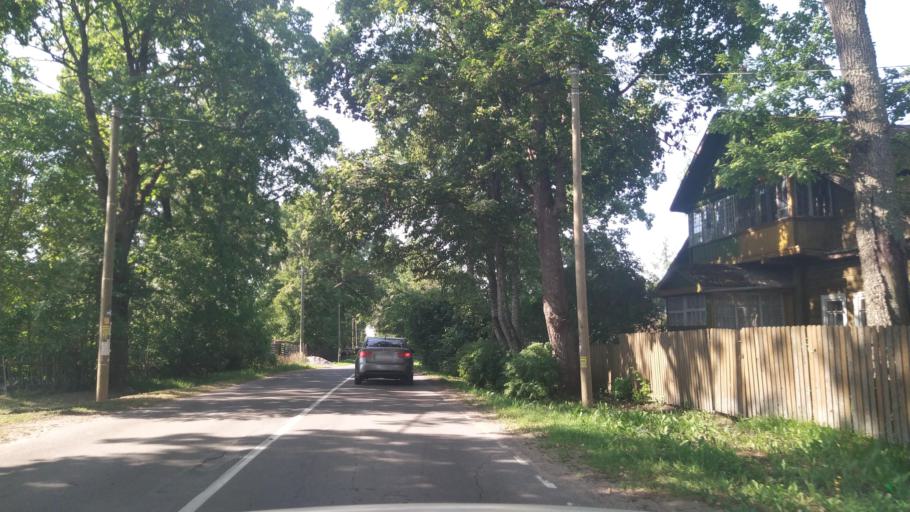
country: RU
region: Leningrad
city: Siverskiy
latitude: 59.2914
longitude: 30.0654
